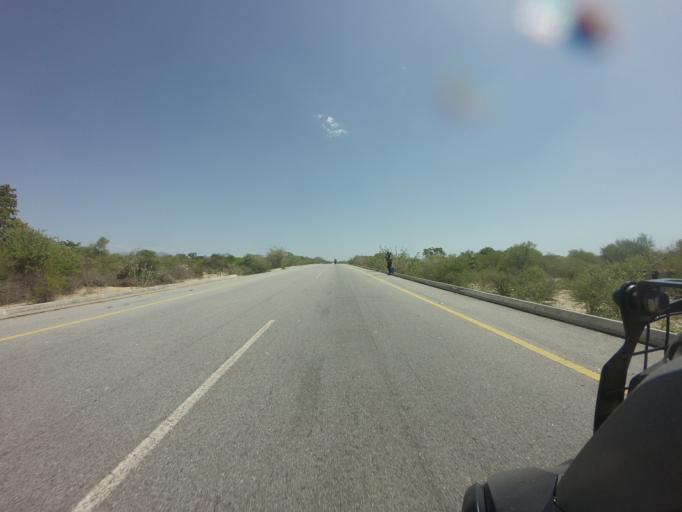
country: AO
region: Benguela
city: Benguela
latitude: -13.1921
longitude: 13.7625
